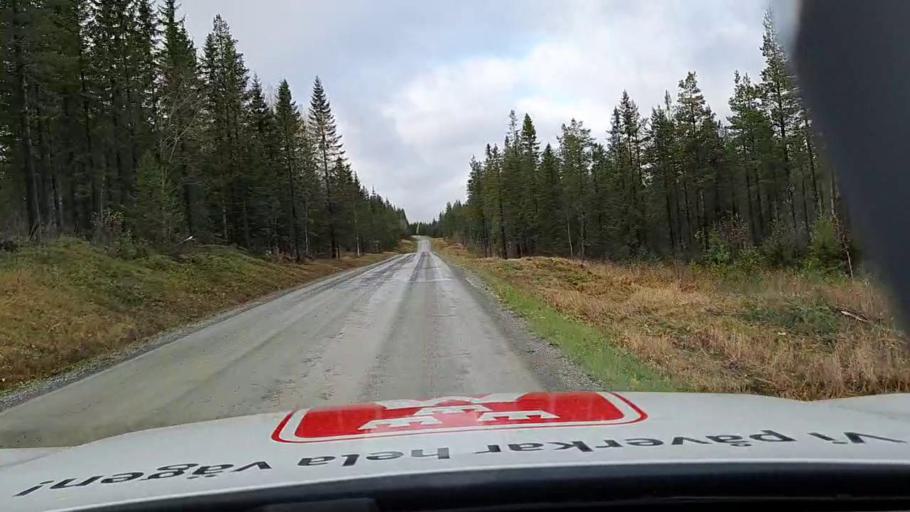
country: SE
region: Jaemtland
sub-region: Bergs Kommun
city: Hoverberg
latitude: 63.0089
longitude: 14.1190
